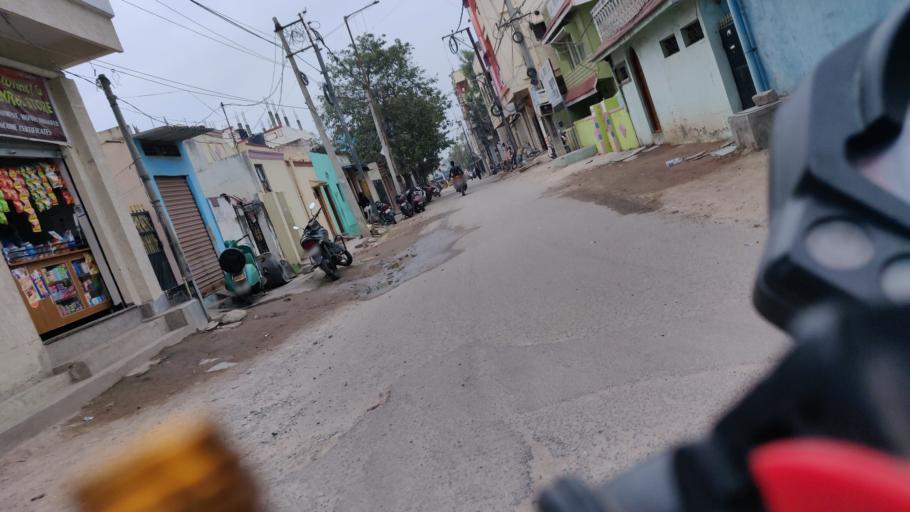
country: IN
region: Telangana
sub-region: Rangareddi
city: Kukatpalli
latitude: 17.4531
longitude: 78.4105
